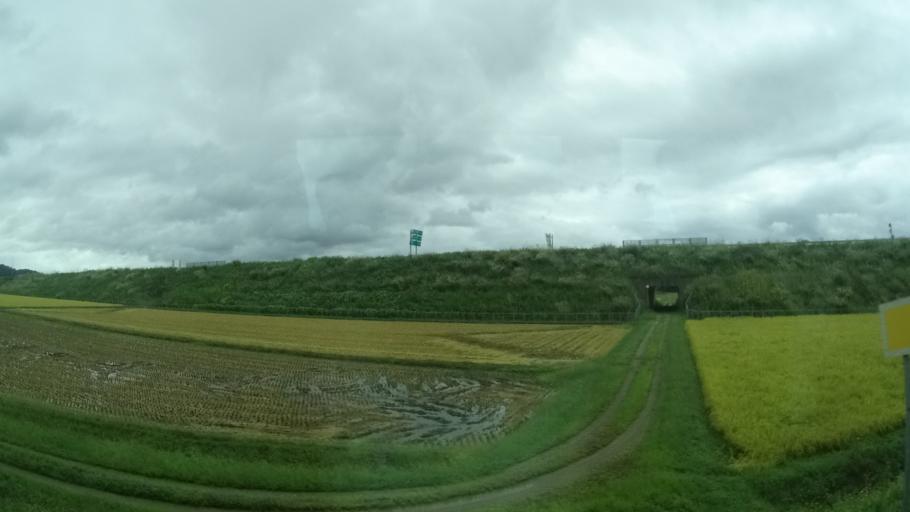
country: JP
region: Niigata
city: Murakami
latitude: 38.1936
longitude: 139.4600
